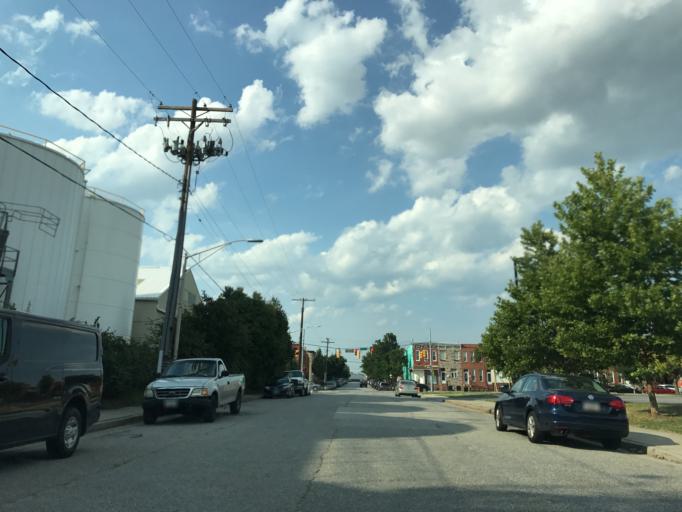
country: US
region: Maryland
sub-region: City of Baltimore
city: Baltimore
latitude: 39.2686
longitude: -76.5955
